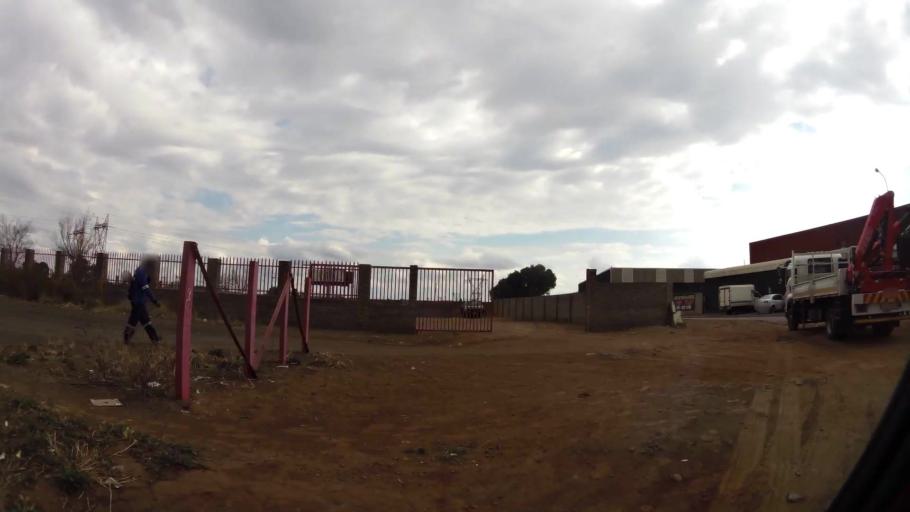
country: ZA
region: Gauteng
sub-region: Sedibeng District Municipality
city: Vanderbijlpark
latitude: -26.6895
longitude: 27.8055
